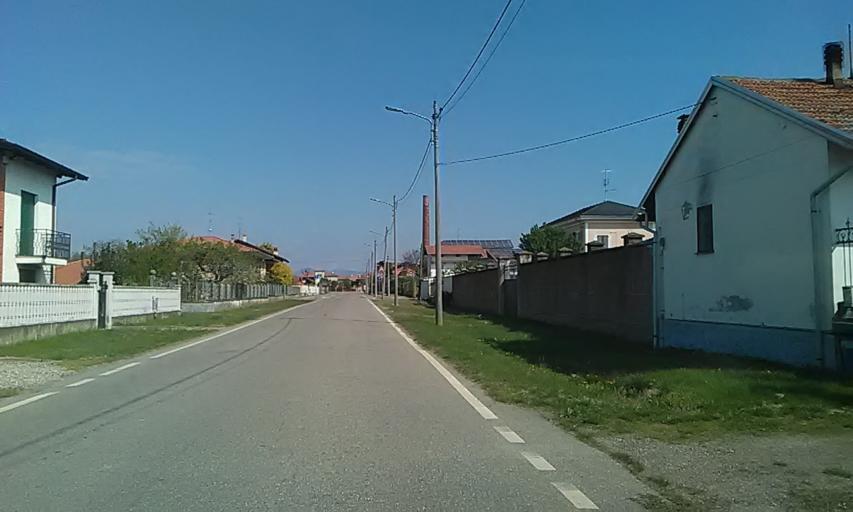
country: IT
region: Piedmont
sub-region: Provincia di Vercelli
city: Lenta
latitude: 45.5502
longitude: 8.3846
